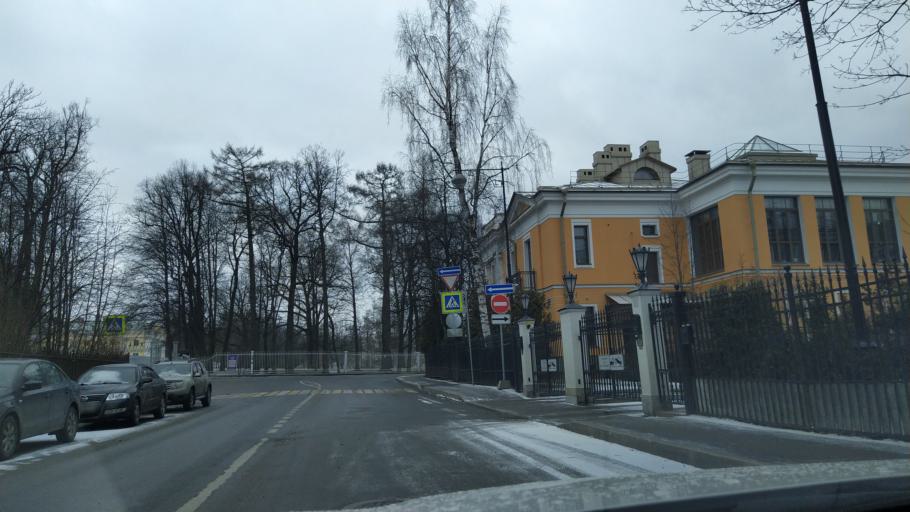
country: RU
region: St.-Petersburg
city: Pushkin
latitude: 59.7210
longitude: 30.3966
